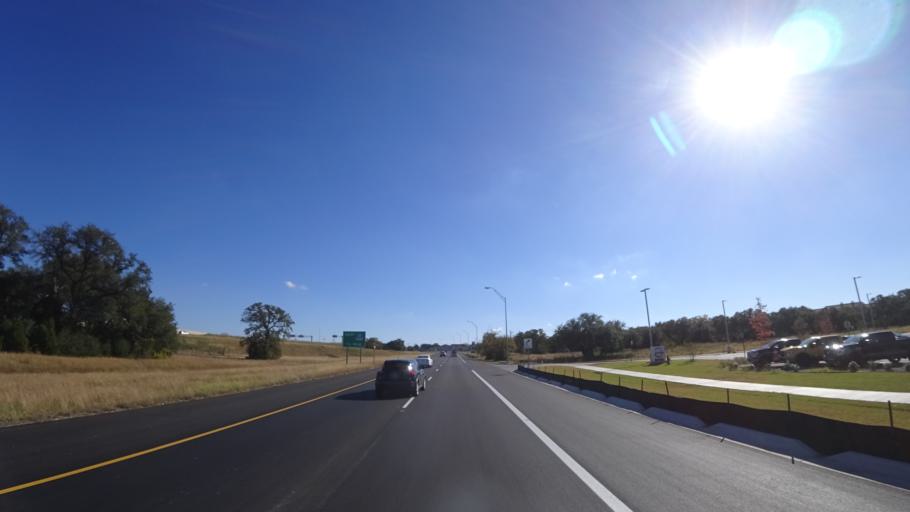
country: US
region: Texas
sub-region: Williamson County
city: Cedar Park
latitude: 30.4848
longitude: -97.8067
